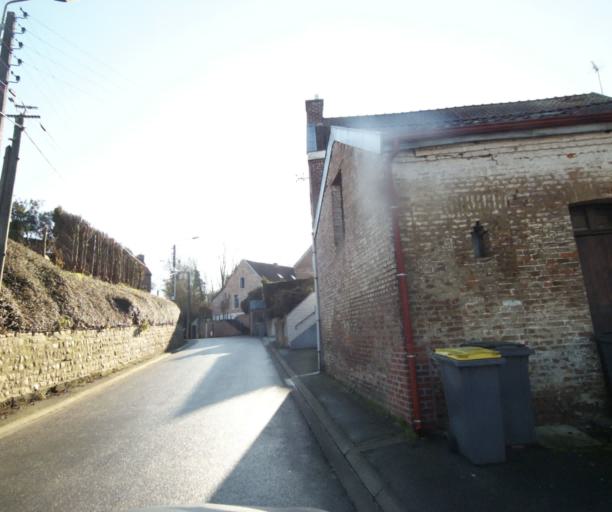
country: FR
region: Nord-Pas-de-Calais
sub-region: Departement du Nord
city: Aulnoy-lez-Valenciennes
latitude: 50.3296
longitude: 3.5341
